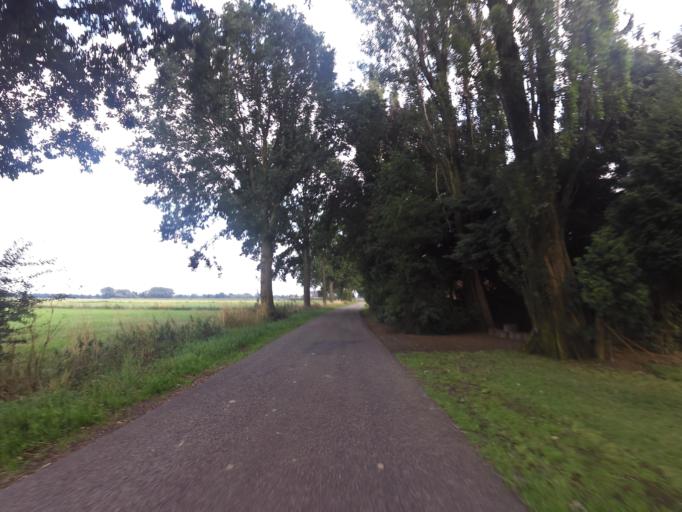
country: NL
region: Gelderland
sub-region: Oude IJsselstreek
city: Gendringen
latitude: 51.9046
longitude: 6.3321
